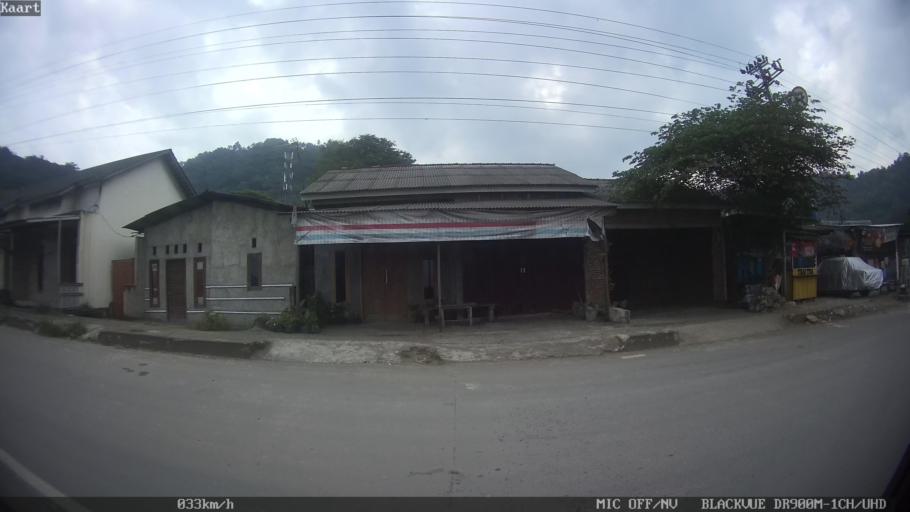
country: ID
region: Lampung
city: Panjang
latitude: -5.4620
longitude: 105.3215
